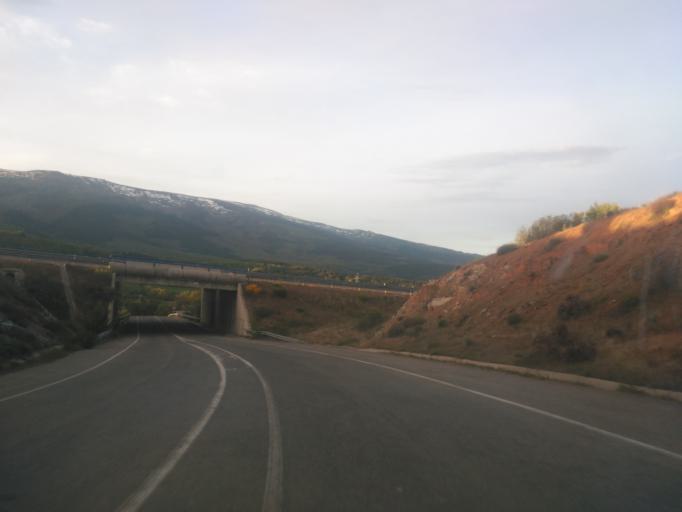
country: ES
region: Castille and Leon
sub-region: Provincia de Salamanca
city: Vallejera de Riofrio
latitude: 40.3991
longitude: -5.7387
